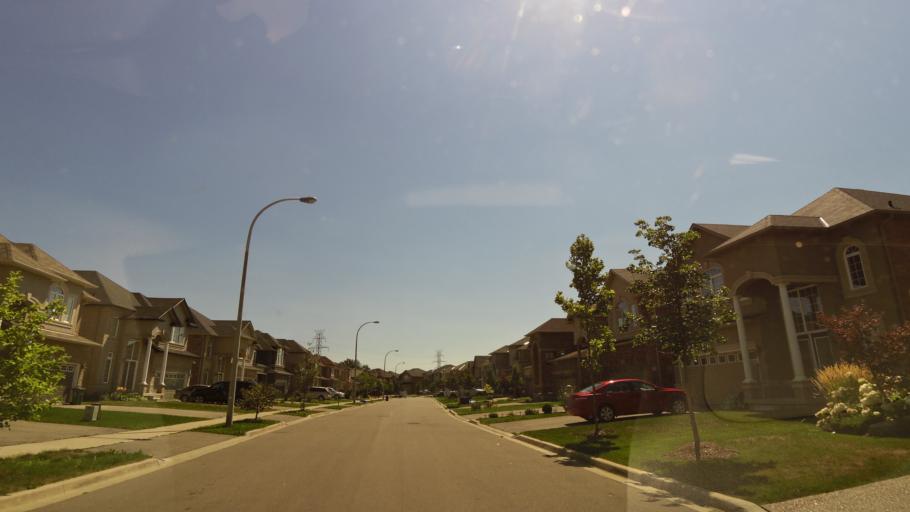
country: CA
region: Ontario
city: Ancaster
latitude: 43.2136
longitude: -79.9447
